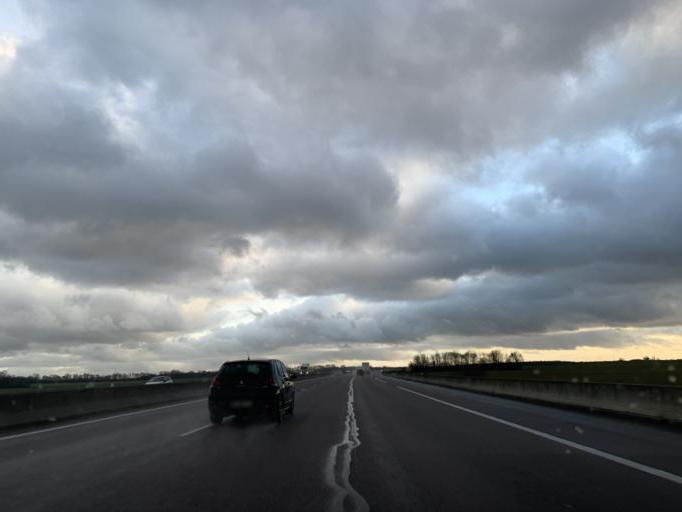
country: FR
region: Champagne-Ardenne
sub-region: Departement de la Haute-Marne
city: Langres
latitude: 47.8490
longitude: 5.2304
